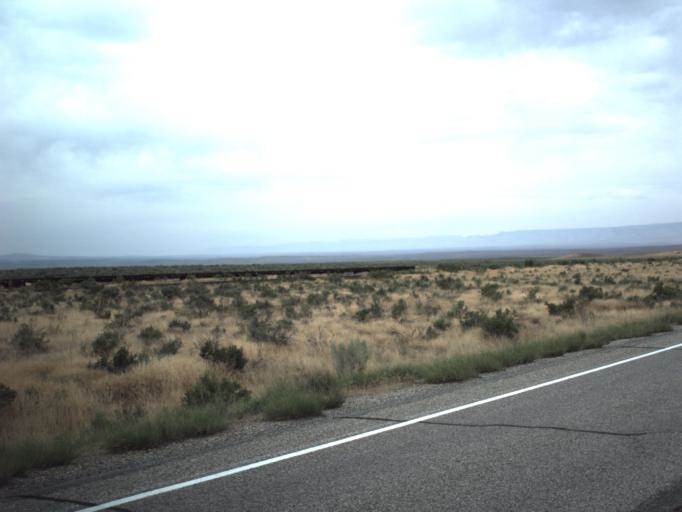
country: US
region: Utah
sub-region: Carbon County
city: East Carbon City
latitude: 39.5360
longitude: -110.4958
